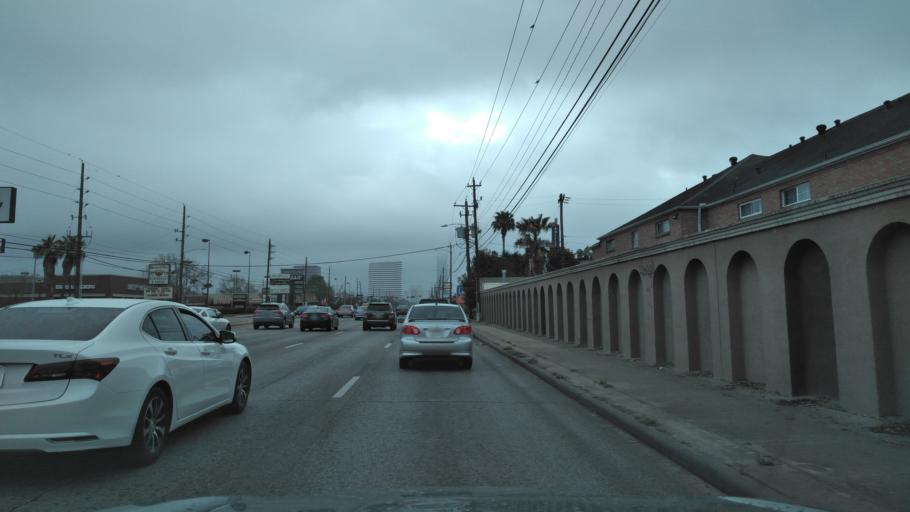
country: US
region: Texas
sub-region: Harris County
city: Hunters Creek Village
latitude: 29.7376
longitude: -95.4927
